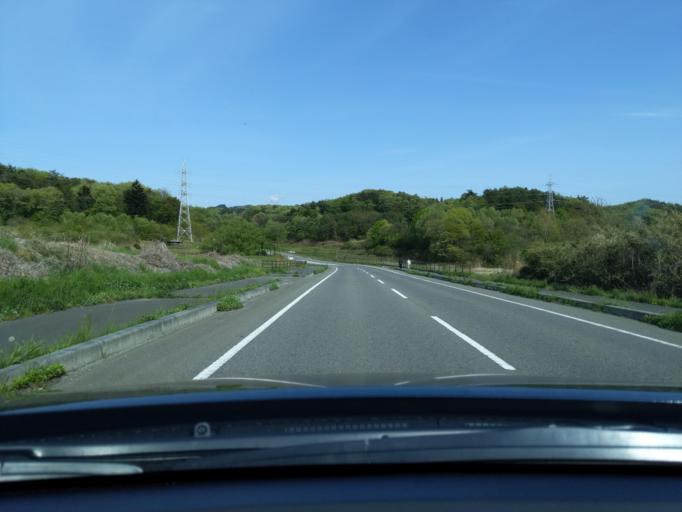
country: JP
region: Fukushima
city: Koriyama
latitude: 37.3544
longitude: 140.4215
